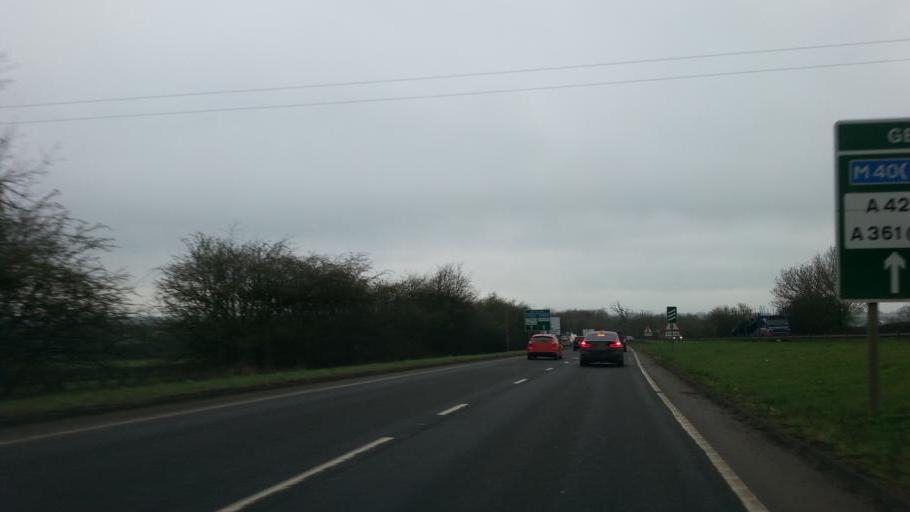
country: GB
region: England
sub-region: Oxfordshire
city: Banbury
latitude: 52.0714
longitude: -1.3066
